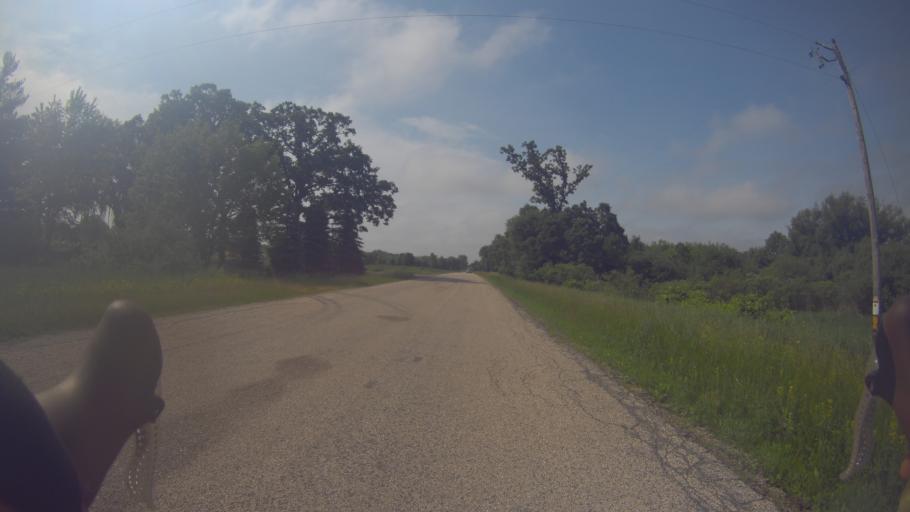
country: US
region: Wisconsin
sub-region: Dane County
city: Stoughton
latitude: 42.9526
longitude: -89.1810
